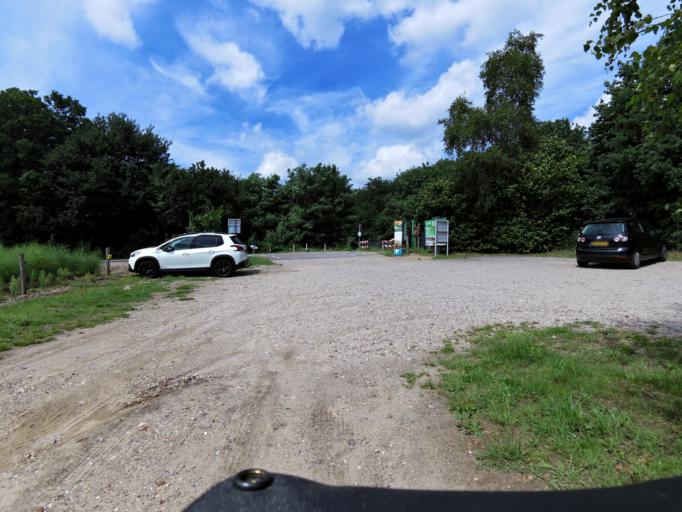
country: NL
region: Limburg
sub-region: Gemeente Roerdalen
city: Vlodrop
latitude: 51.1602
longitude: 6.1007
